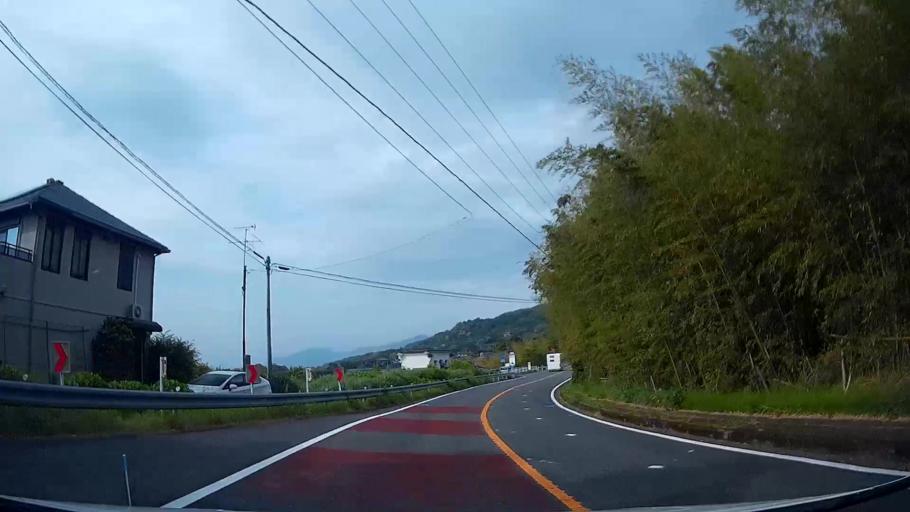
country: JP
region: Shizuoka
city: Heda
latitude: 34.8704
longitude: 138.7613
